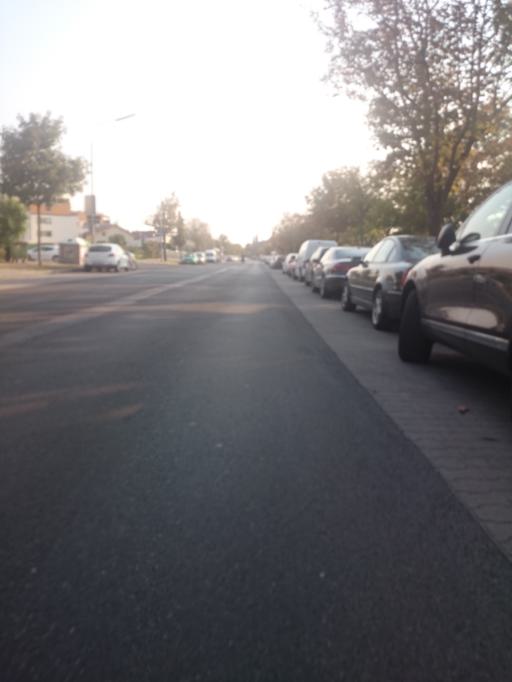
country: AT
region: Lower Austria
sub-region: Politischer Bezirk Wien-Umgebung
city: Gerasdorf bei Wien
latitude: 48.2661
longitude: 16.4270
